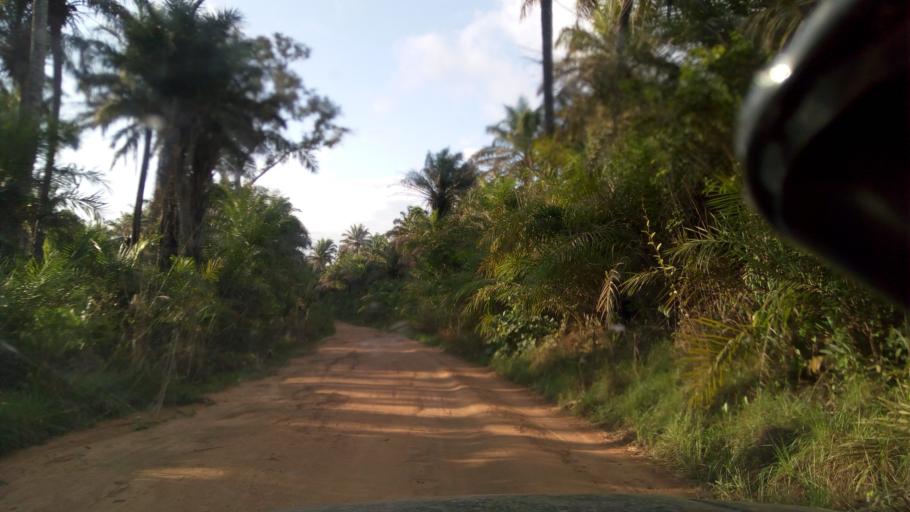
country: SL
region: Northern Province
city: Konakridee
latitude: 8.7622
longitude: -13.1397
